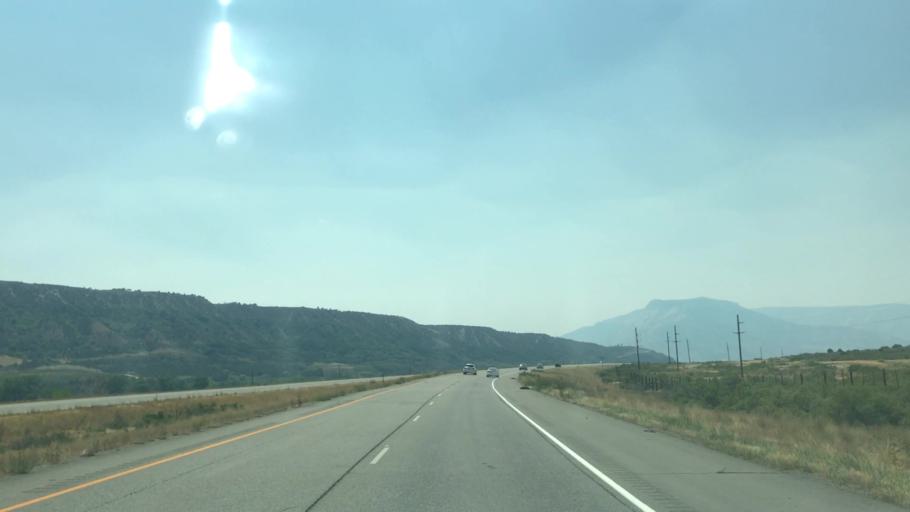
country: US
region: Colorado
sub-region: Garfield County
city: Battlement Mesa
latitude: 39.4803
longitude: -107.9718
